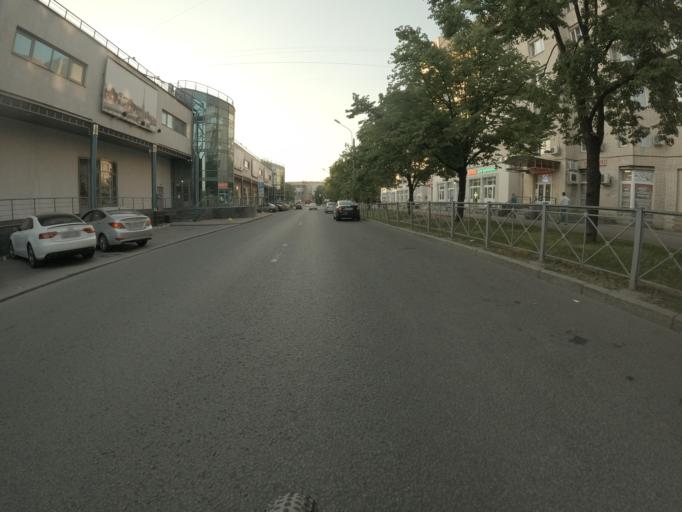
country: RU
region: St.-Petersburg
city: Dachnoye
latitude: 59.8503
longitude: 30.2689
